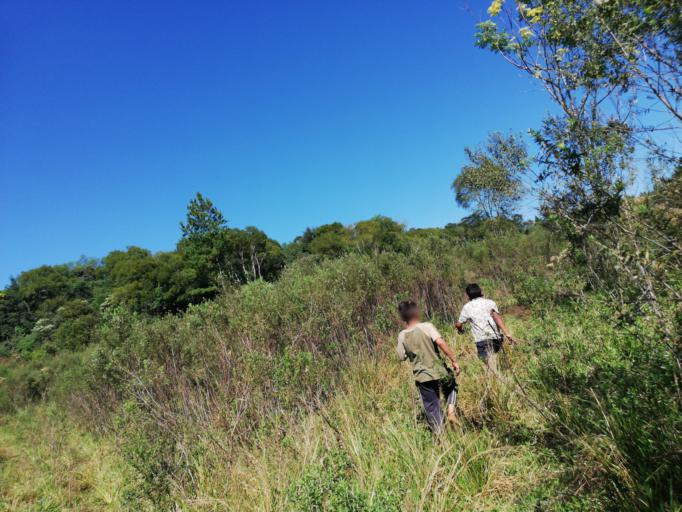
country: AR
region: Misiones
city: El Soberbio
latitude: -27.0620
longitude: -54.3759
